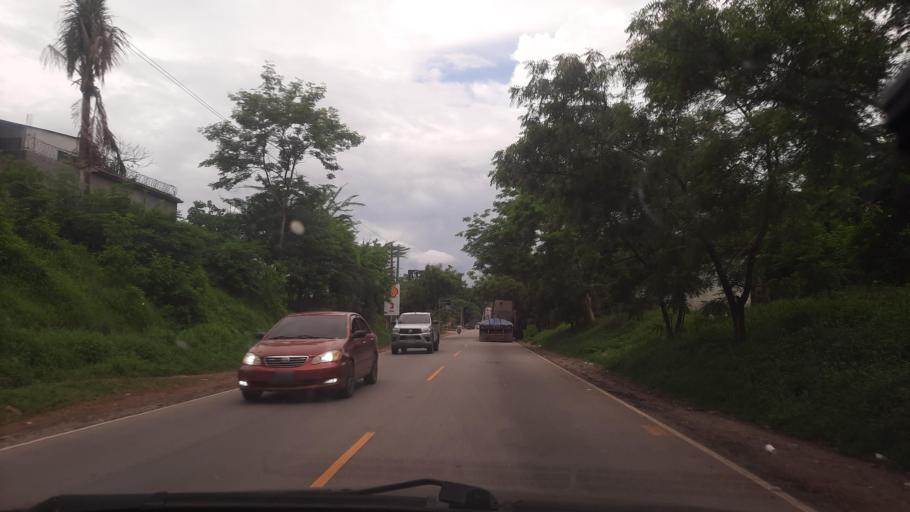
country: GT
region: Chiquimula
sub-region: Municipio de Chiquimula
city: Chiquimula
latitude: 14.8467
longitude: -89.5172
